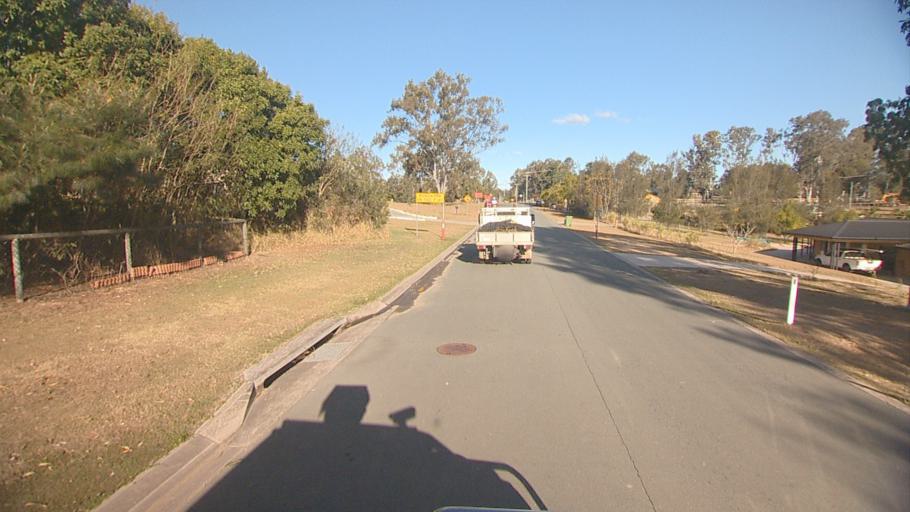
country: AU
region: Queensland
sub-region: Logan
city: Cedar Vale
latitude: -27.8307
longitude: 153.0045
